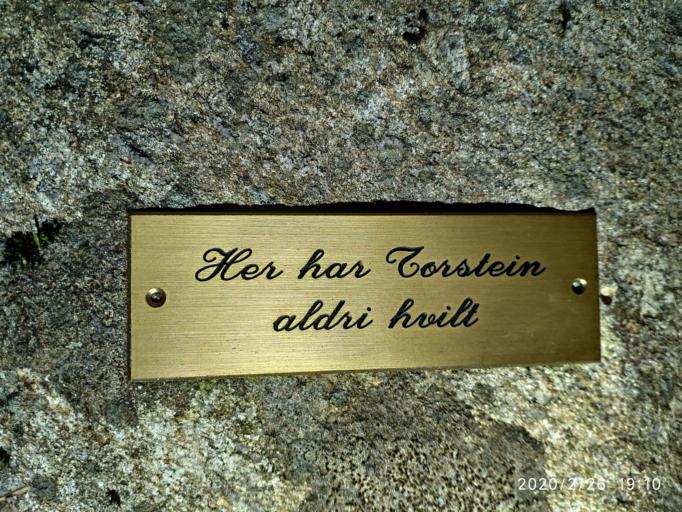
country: NO
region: Hordaland
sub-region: Tysnes
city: Uggdal
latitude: 60.0160
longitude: 5.5369
